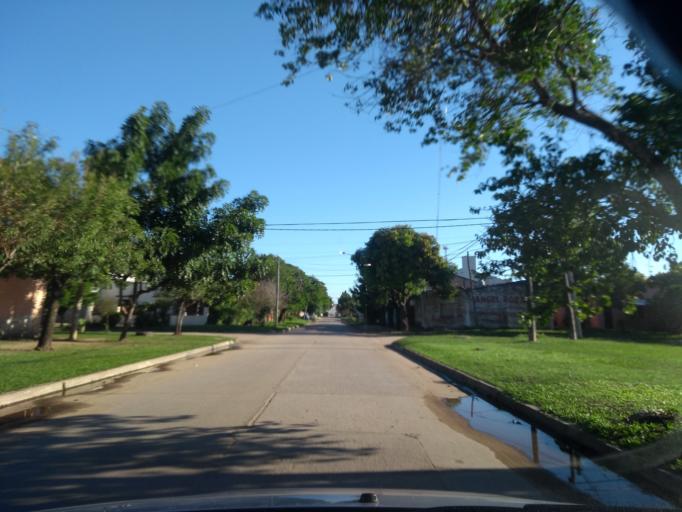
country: AR
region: Chaco
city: Barranqueras
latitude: -27.4812
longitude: -58.9378
